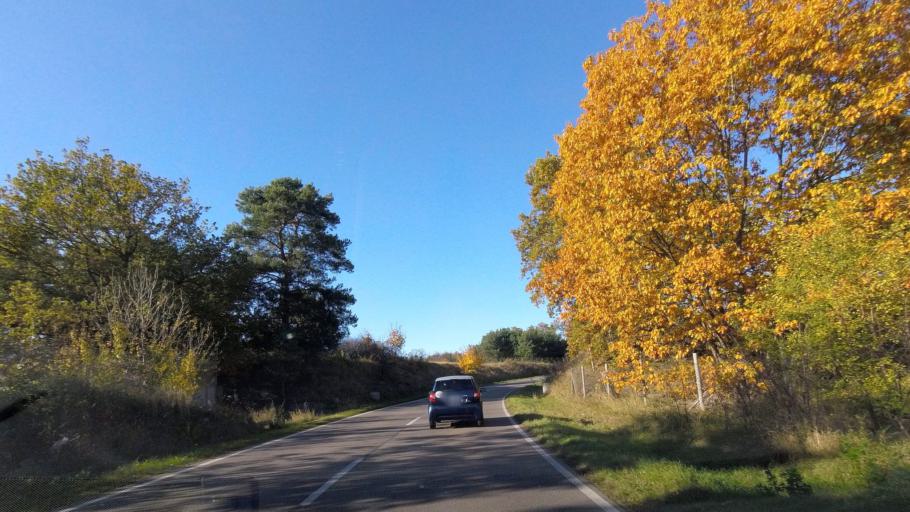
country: DE
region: Saxony-Anhalt
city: Zahna
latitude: 51.9233
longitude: 12.7835
